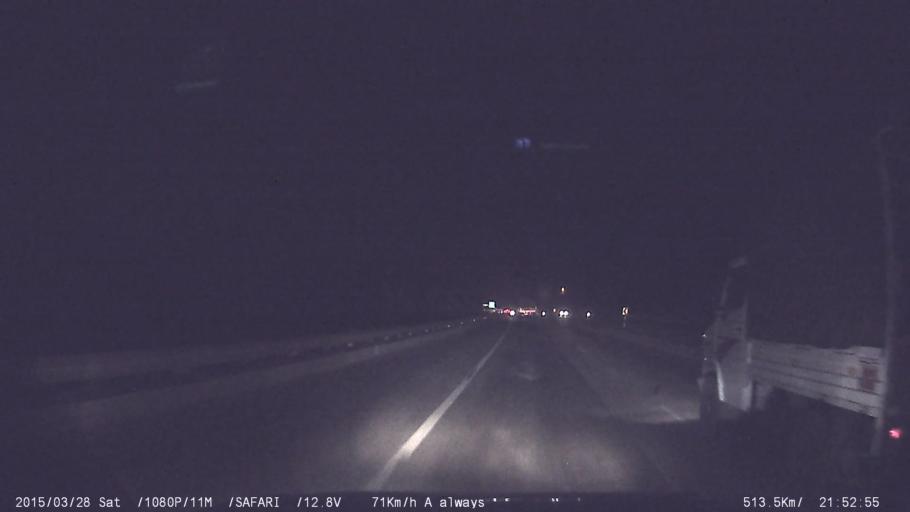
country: IN
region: Karnataka
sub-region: Bangalore Urban
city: Bangalore
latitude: 12.8523
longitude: 77.5465
